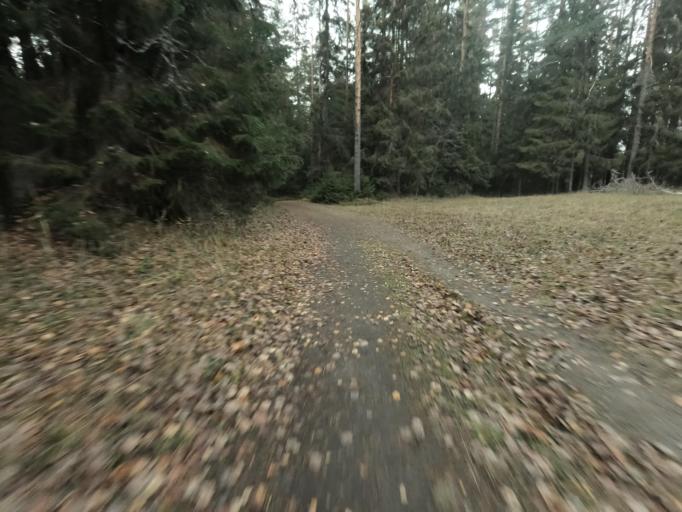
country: RU
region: Leningrad
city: Leninskoye
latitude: 60.1968
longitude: 29.8481
